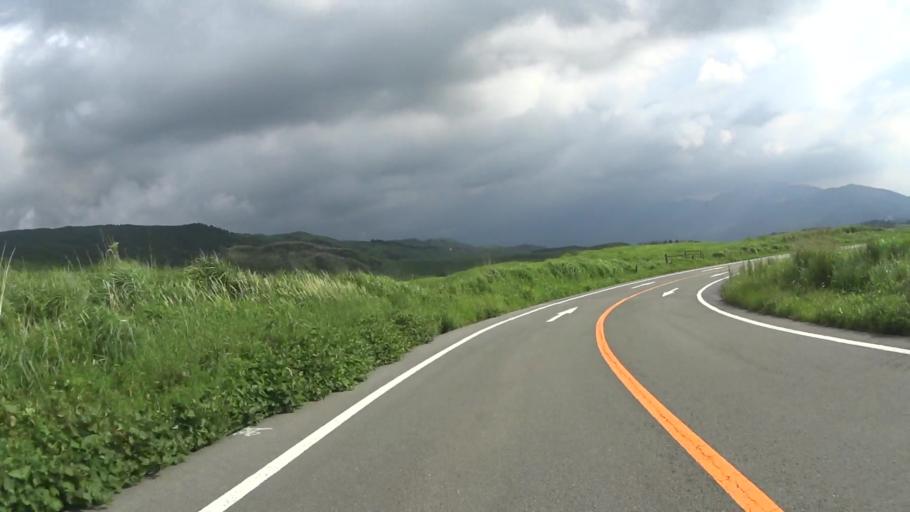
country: JP
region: Kumamoto
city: Aso
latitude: 32.9031
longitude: 131.0346
